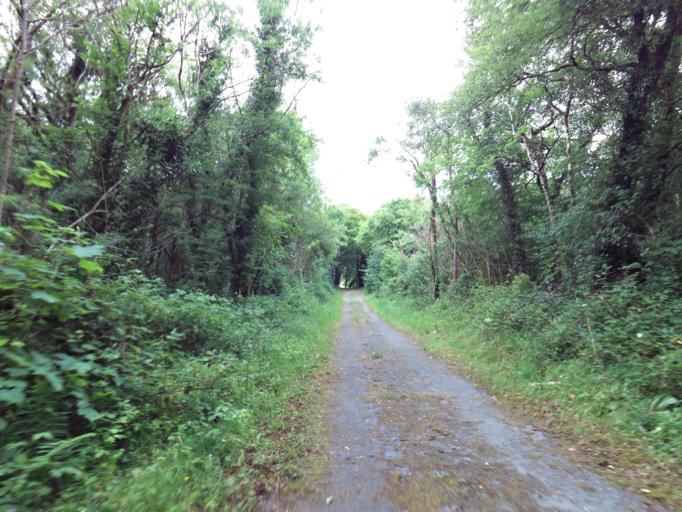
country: IE
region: Connaught
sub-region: County Galway
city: Gort
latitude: 53.0873
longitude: -8.8680
